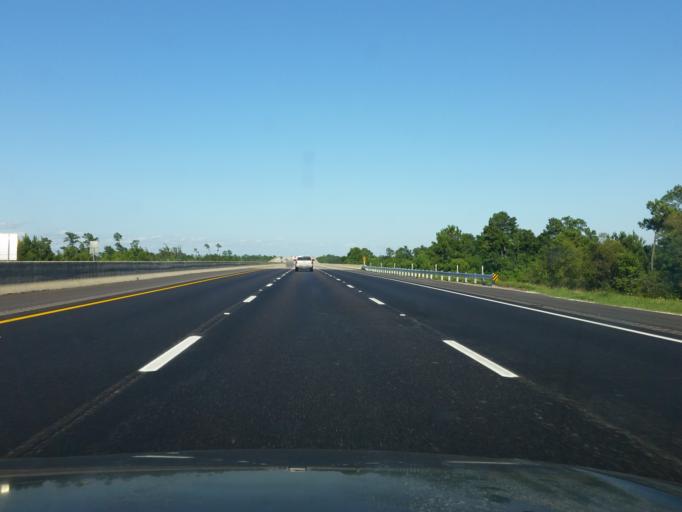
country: US
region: Mississippi
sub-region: Hancock County
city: Kiln
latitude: 30.3622
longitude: -89.4105
